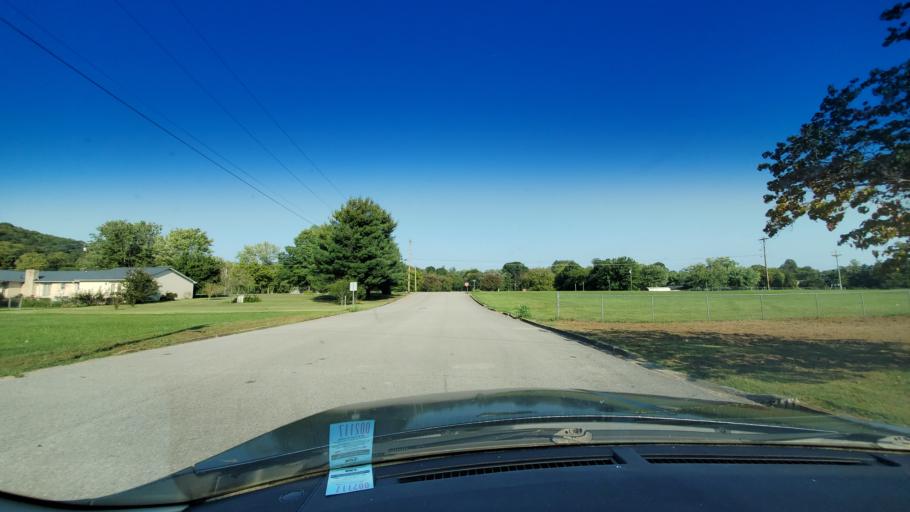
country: US
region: Tennessee
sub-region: Smith County
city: Carthage
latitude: 36.2593
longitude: -85.9571
